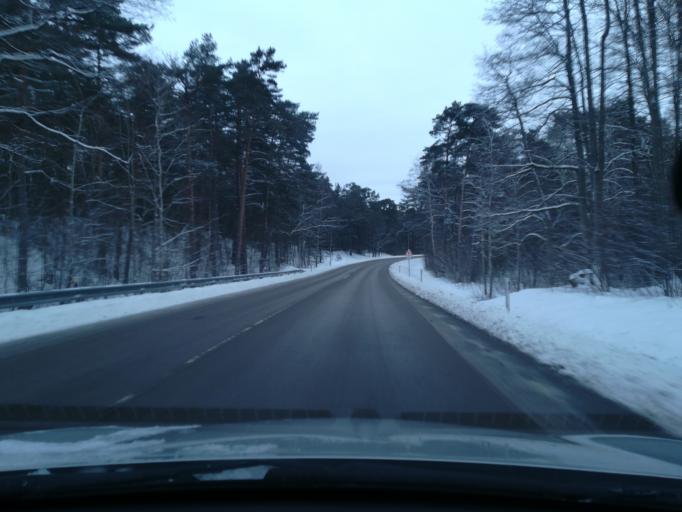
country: EE
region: Harju
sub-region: Keila linn
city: Keila
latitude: 59.4090
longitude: 24.2975
